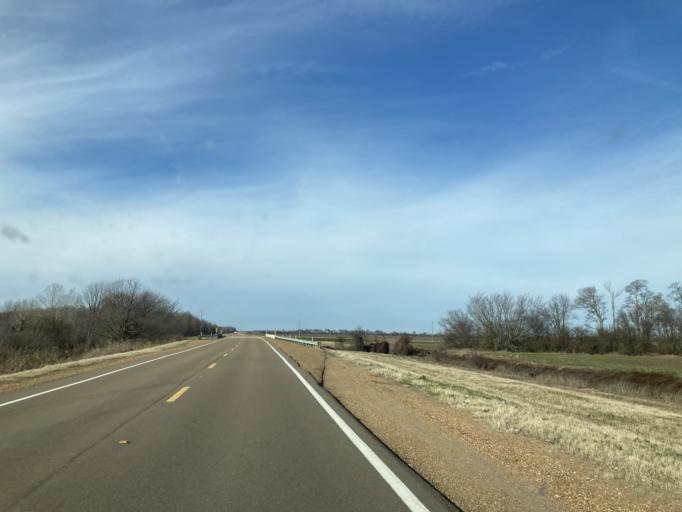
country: US
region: Mississippi
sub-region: Humphreys County
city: Belzoni
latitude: 32.9956
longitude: -90.6193
